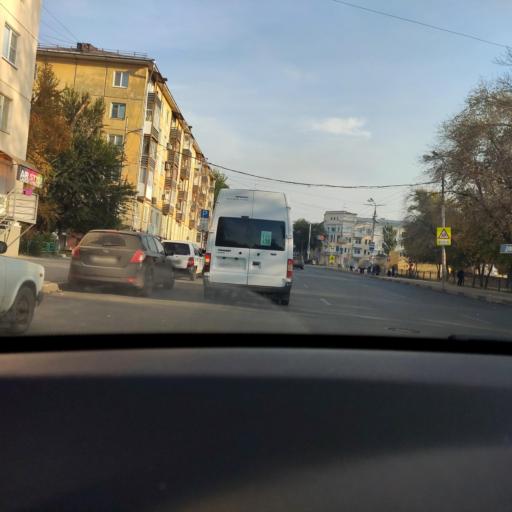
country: RU
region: Samara
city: Samara
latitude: 53.1905
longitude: 50.1238
